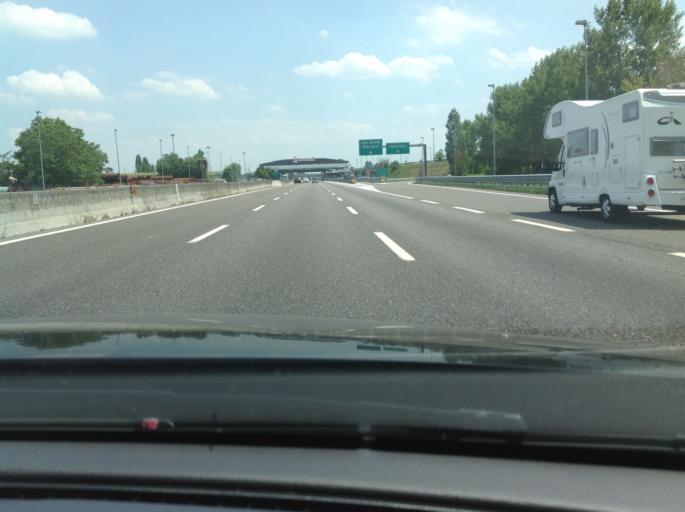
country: IT
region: Emilia-Romagna
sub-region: Provincia di Piacenza
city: Cortemaggiore
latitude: 44.9647
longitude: 9.9004
